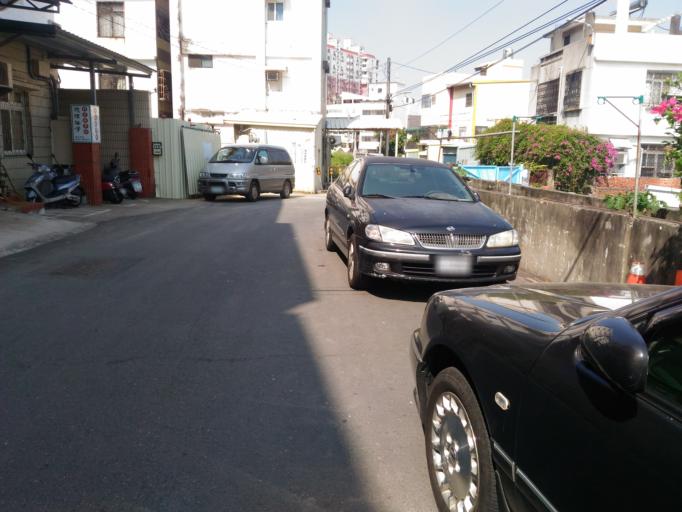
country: TW
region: Taiwan
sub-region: Changhua
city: Chang-hua
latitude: 24.0821
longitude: 120.5521
